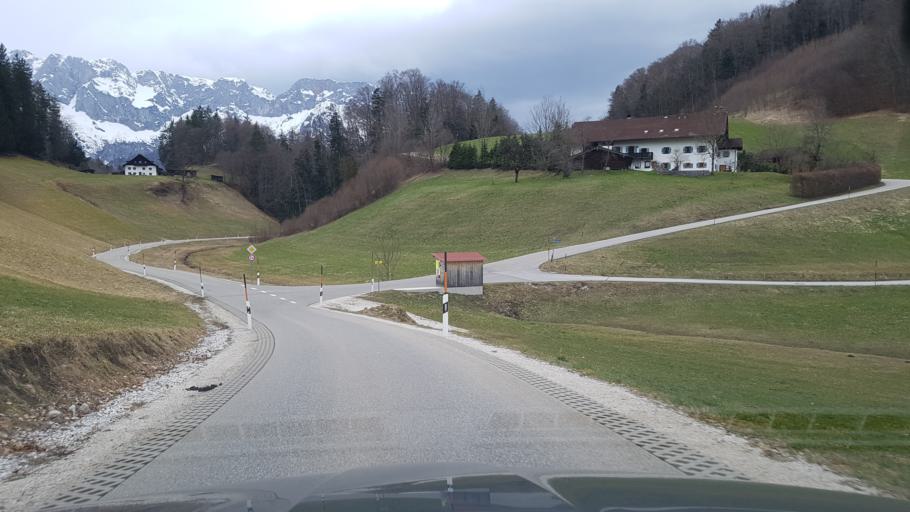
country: DE
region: Bavaria
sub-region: Upper Bavaria
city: Marktschellenberg
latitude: 47.6813
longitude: 13.0663
